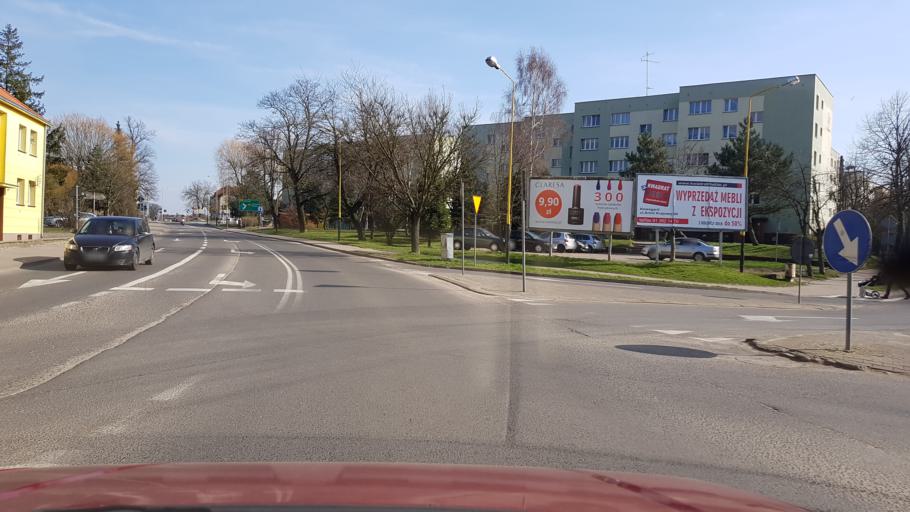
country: PL
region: West Pomeranian Voivodeship
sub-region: Powiat goleniowski
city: Nowogard
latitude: 53.6670
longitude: 15.1253
